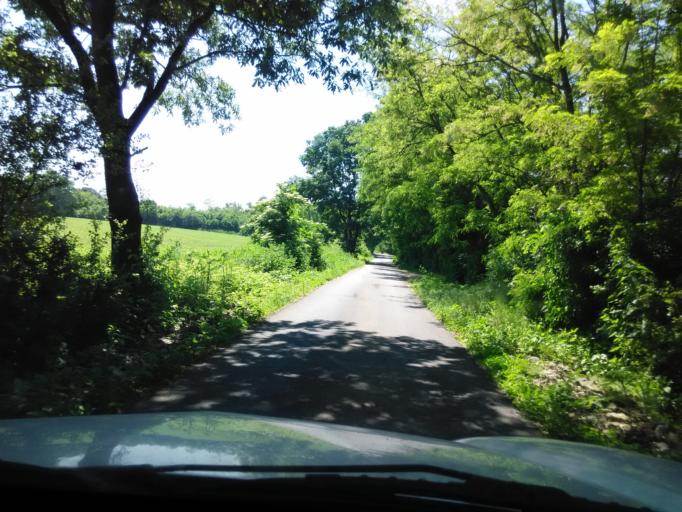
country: SK
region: Nitriansky
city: Tlmace
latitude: 48.2423
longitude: 18.4629
